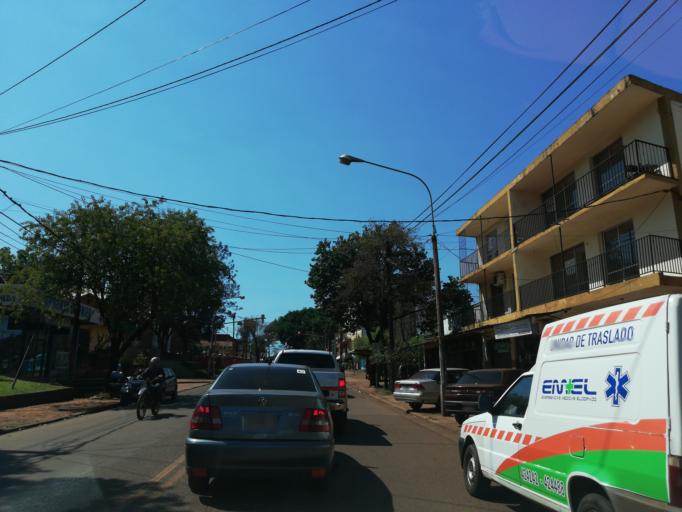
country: AR
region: Misiones
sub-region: Departamento de Eldorado
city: Eldorado
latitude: -26.4040
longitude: -54.6230
